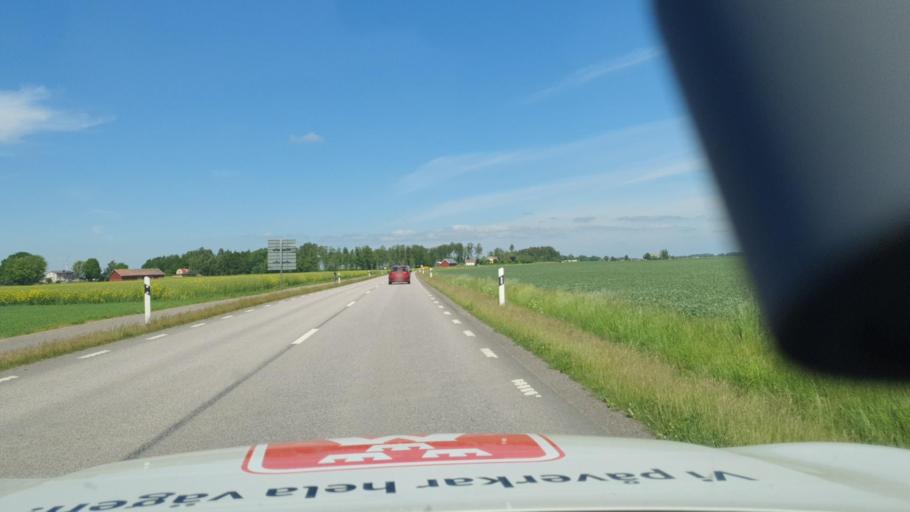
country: SE
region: Vaestra Goetaland
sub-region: Vara Kommun
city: Vara
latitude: 58.2747
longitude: 12.9546
